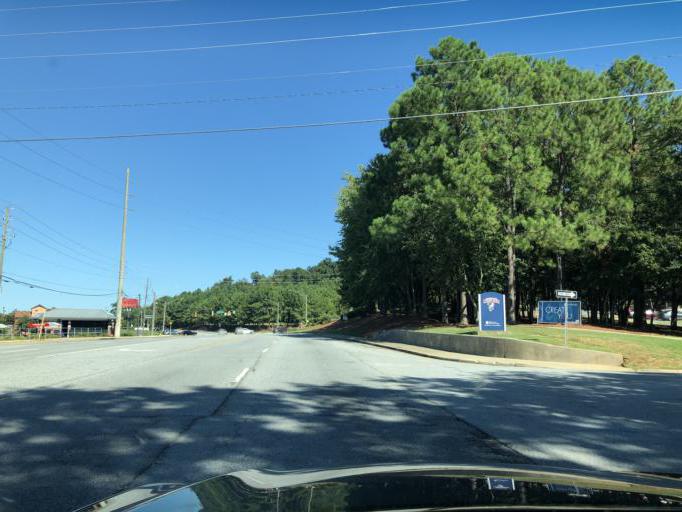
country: US
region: Georgia
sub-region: Muscogee County
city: Columbus
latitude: 32.5056
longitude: -84.9412
